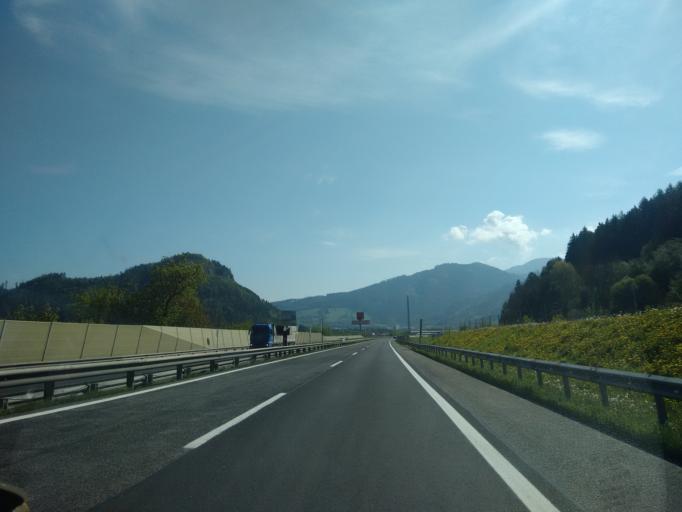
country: AT
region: Styria
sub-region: Politischer Bezirk Leoben
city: Leoben
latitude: 47.3533
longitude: 15.0688
